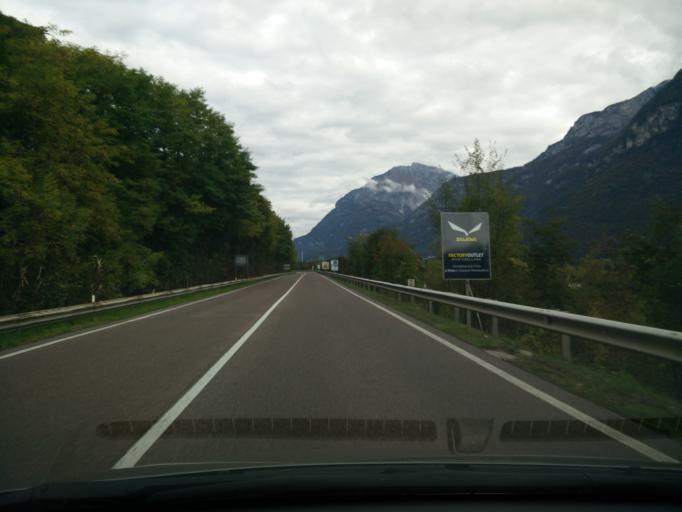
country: IT
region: Veneto
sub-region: Provincia di Belluno
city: Soverzene
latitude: 46.2121
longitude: 12.2871
